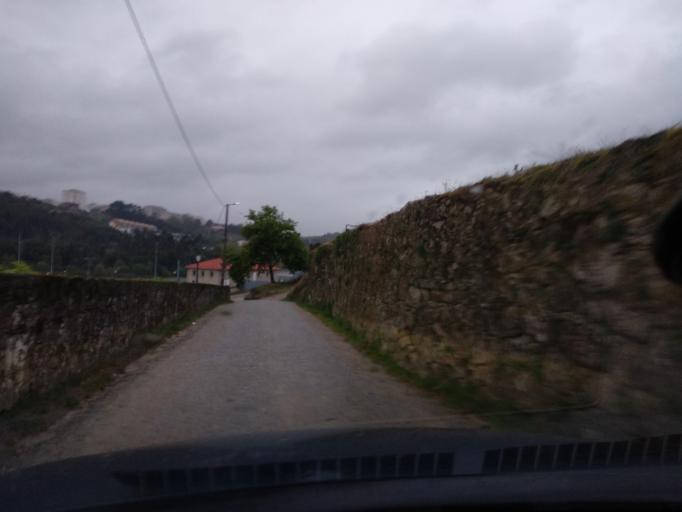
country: PT
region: Porto
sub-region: Penafiel
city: Penafiel
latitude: 41.1895
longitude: -8.2936
